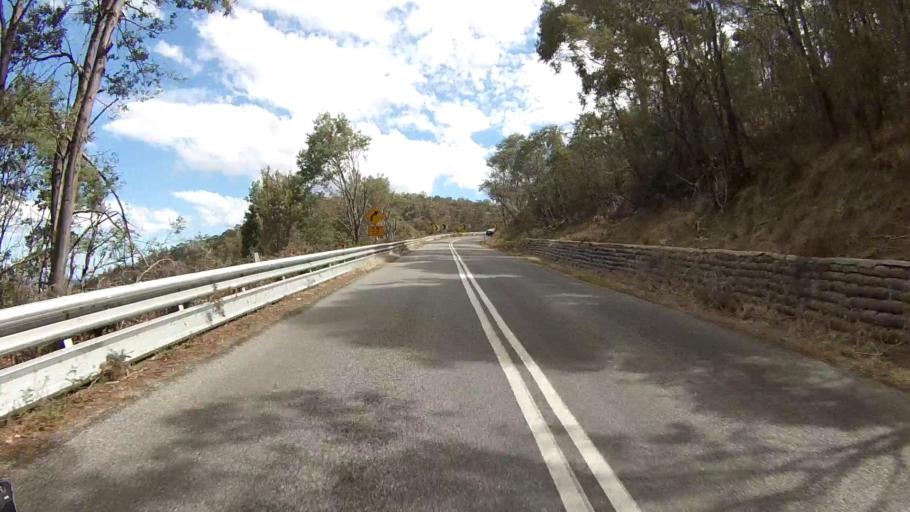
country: AU
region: Tasmania
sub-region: Break O'Day
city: St Helens
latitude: -41.9744
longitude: 148.1499
